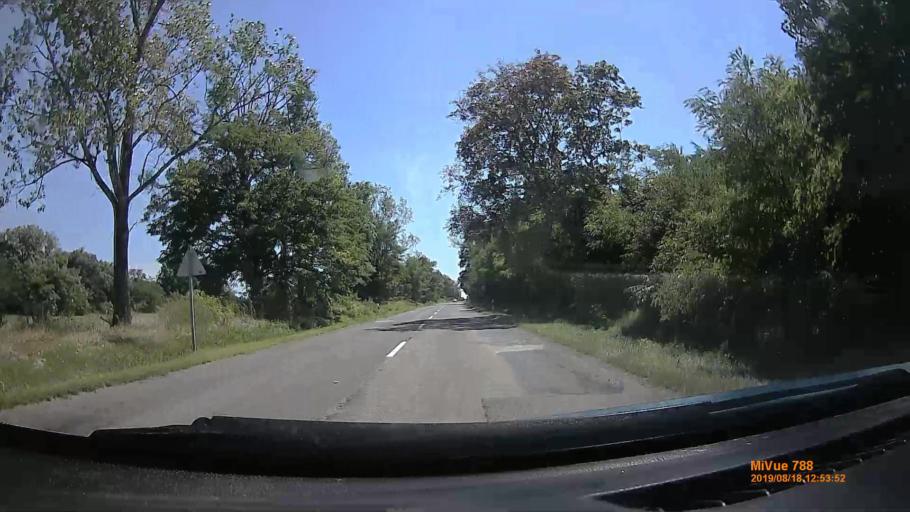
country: HU
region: Fejer
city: Aba
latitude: 47.0468
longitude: 18.5273
